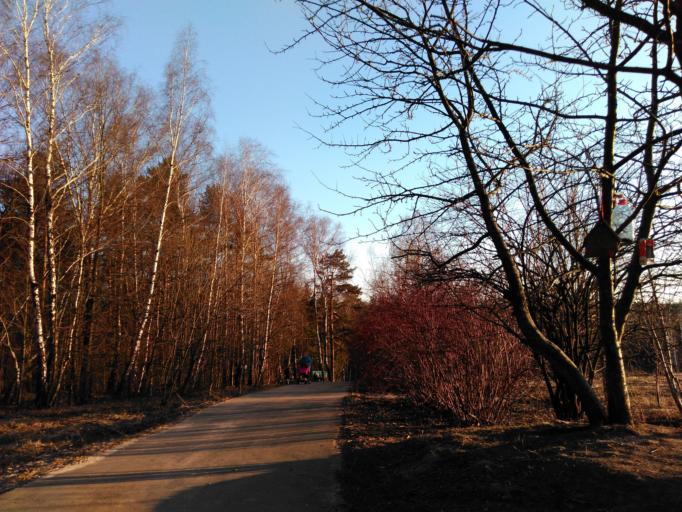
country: RU
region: Moscow
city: Zyuzino
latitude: 55.6340
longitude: 37.5616
